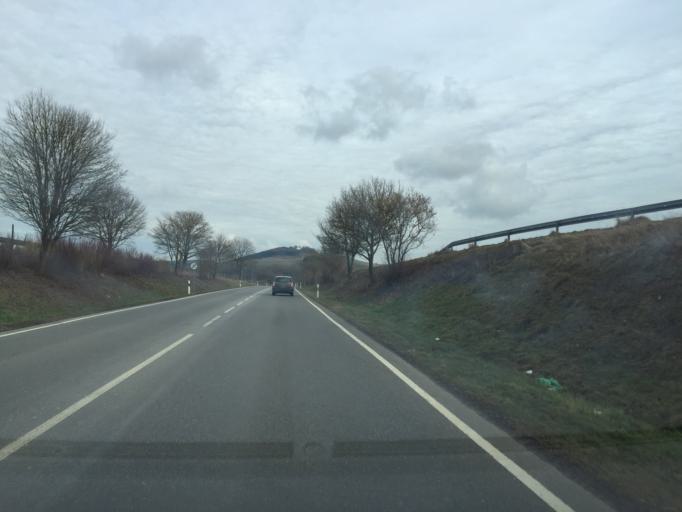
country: DE
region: Baden-Wuerttemberg
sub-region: Freiburg Region
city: Geisingen
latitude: 47.9269
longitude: 8.5782
